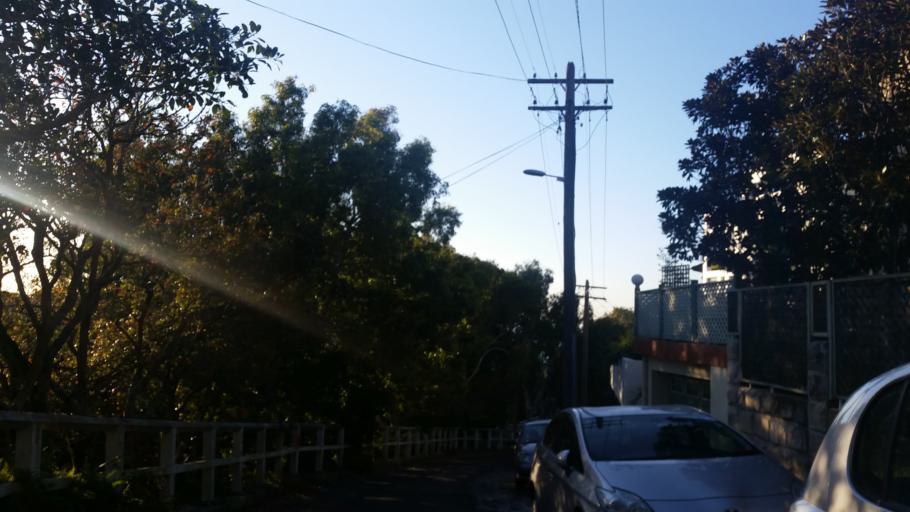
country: AU
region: New South Wales
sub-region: Waverley
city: Bronte
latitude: -33.9025
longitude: 151.2641
